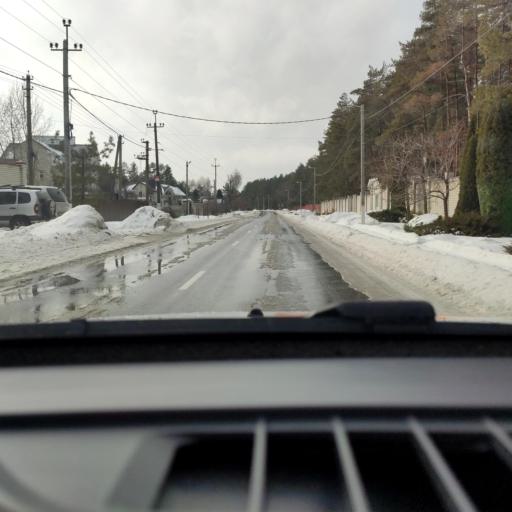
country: RU
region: Voronezj
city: Podgornoye
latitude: 51.7841
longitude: 39.1421
